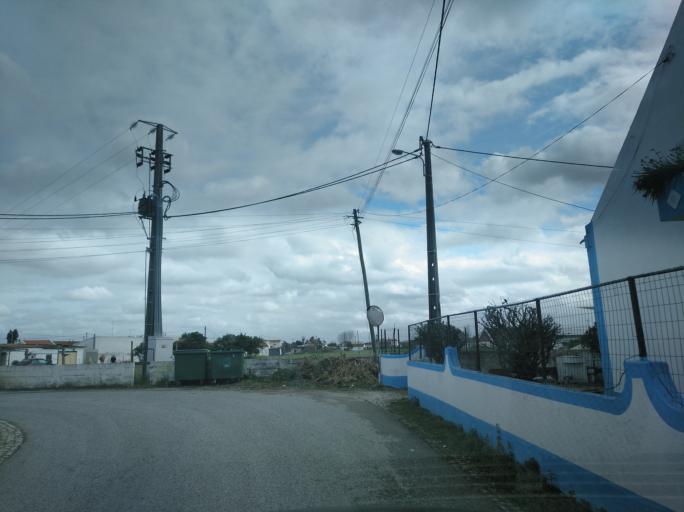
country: PT
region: Setubal
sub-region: Palmela
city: Pinhal Novo
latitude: 38.6737
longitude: -8.9198
